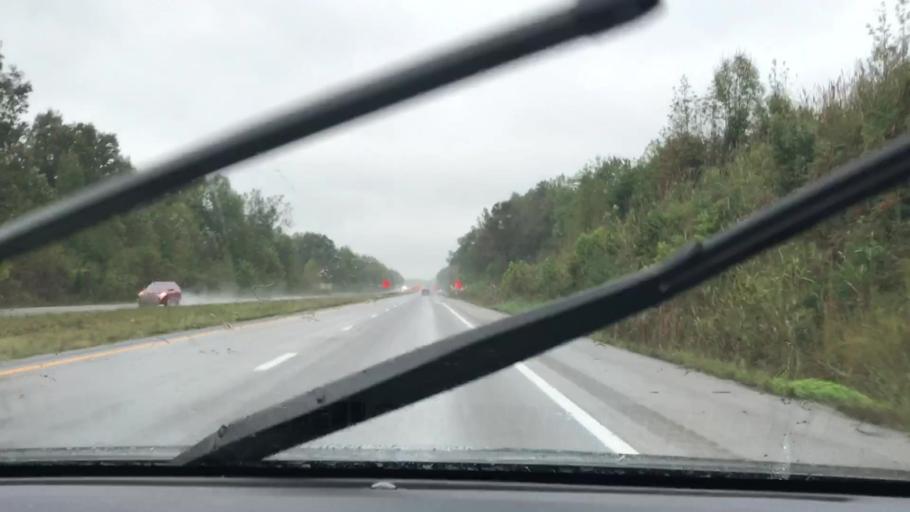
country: US
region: Kentucky
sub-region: Hopkins County
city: Nortonville
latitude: 37.1659
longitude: -87.4544
